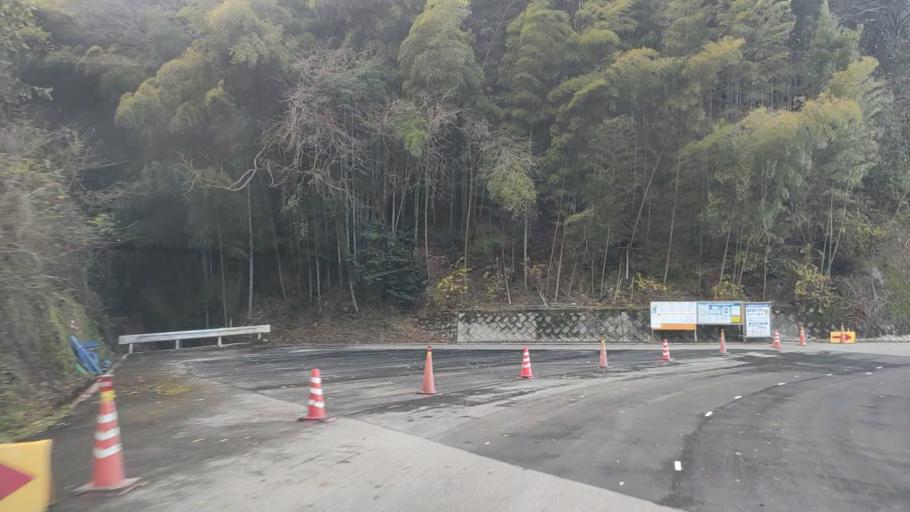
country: JP
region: Ehime
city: Saijo
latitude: 33.8787
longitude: 133.1338
